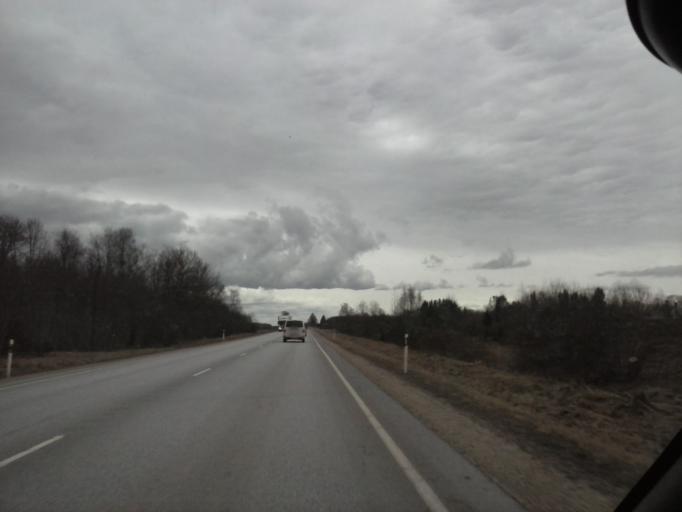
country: EE
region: Jaervamaa
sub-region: Paide linn
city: Paide
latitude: 58.7960
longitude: 25.7580
